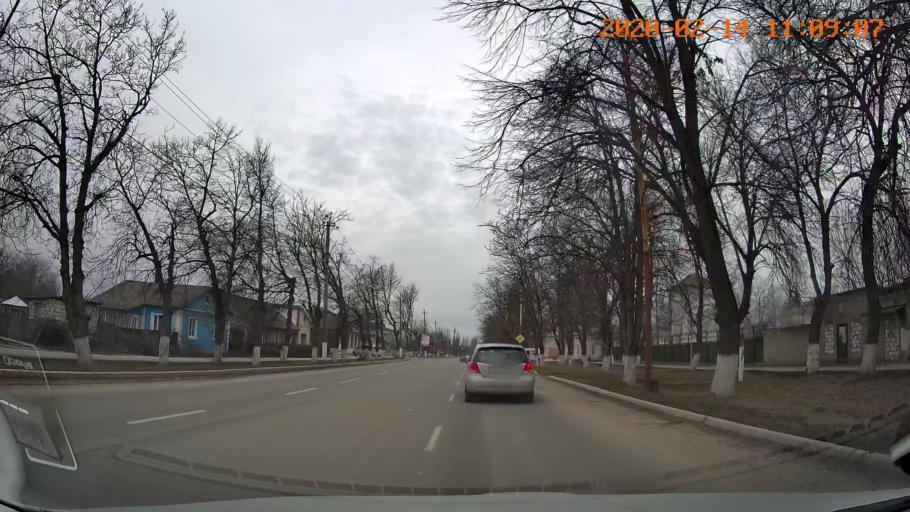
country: MD
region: Raionul Edinet
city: Edinet
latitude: 48.1762
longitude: 27.2964
